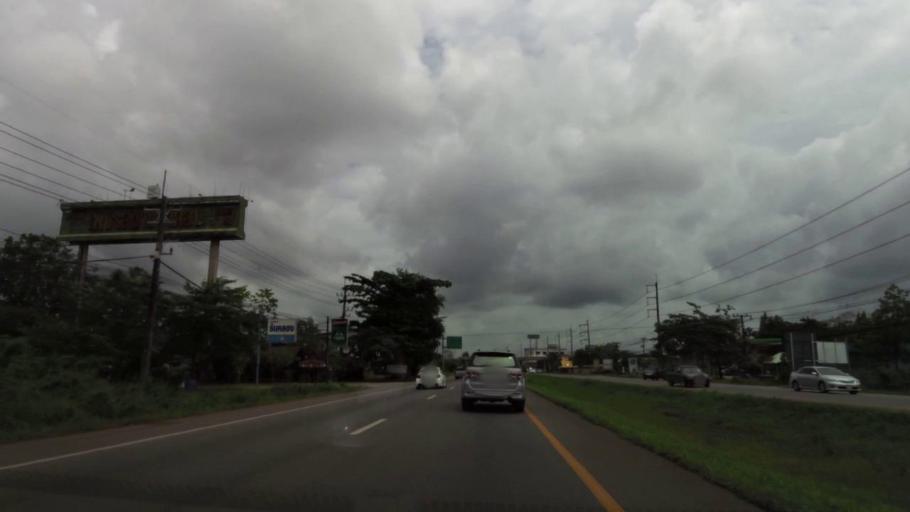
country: TH
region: Chanthaburi
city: Na Yai Am
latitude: 12.7643
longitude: 101.8526
